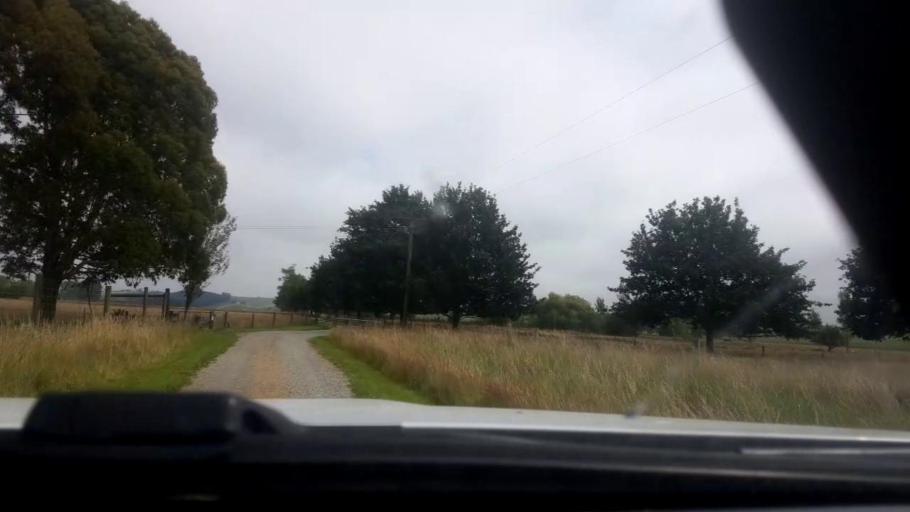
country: NZ
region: Canterbury
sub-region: Timaru District
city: Pleasant Point
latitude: -44.3233
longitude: 171.1933
